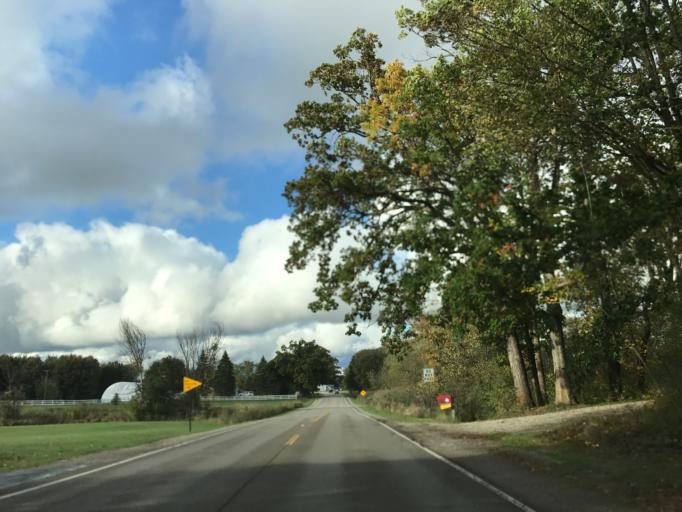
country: US
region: Michigan
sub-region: Oakland County
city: South Lyon
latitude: 42.4207
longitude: -83.6468
